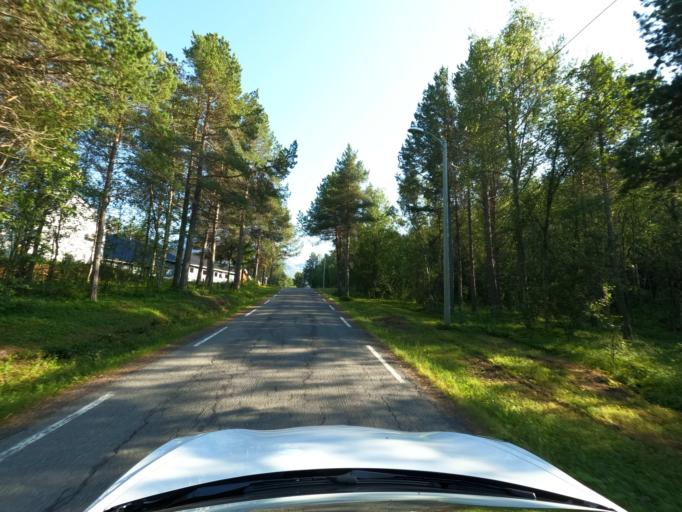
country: NO
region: Nordland
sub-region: Narvik
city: Bjerkvik
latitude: 68.4794
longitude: 17.5278
